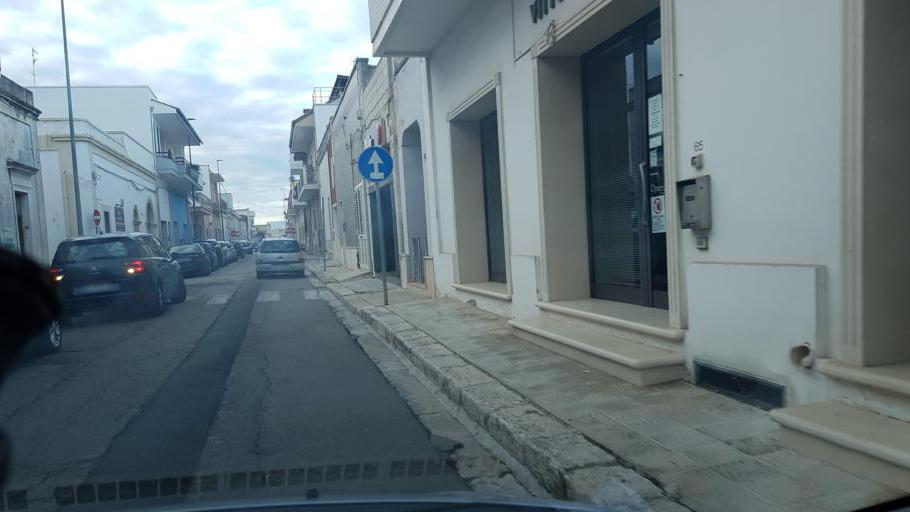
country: IT
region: Apulia
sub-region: Provincia di Lecce
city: Veglie
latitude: 40.3338
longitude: 17.9663
